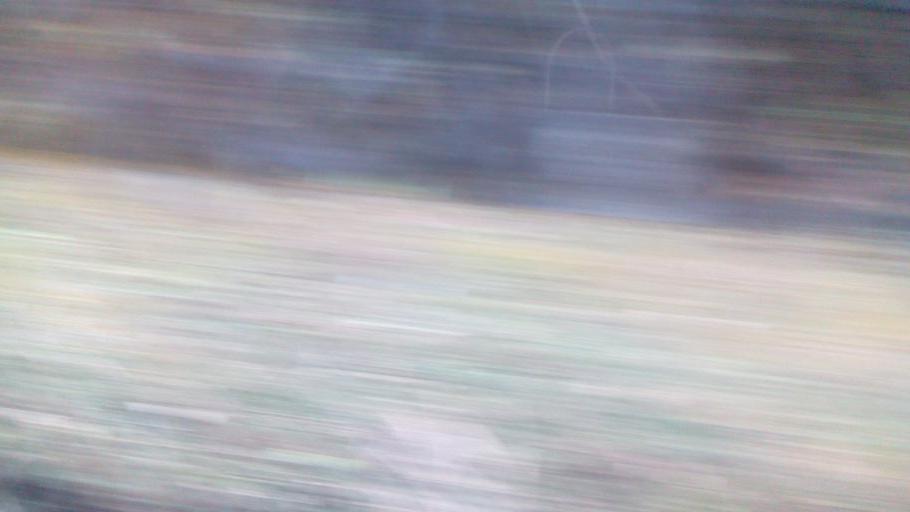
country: TW
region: Taiwan
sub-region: Yilan
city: Yilan
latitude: 24.5453
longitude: 121.4583
